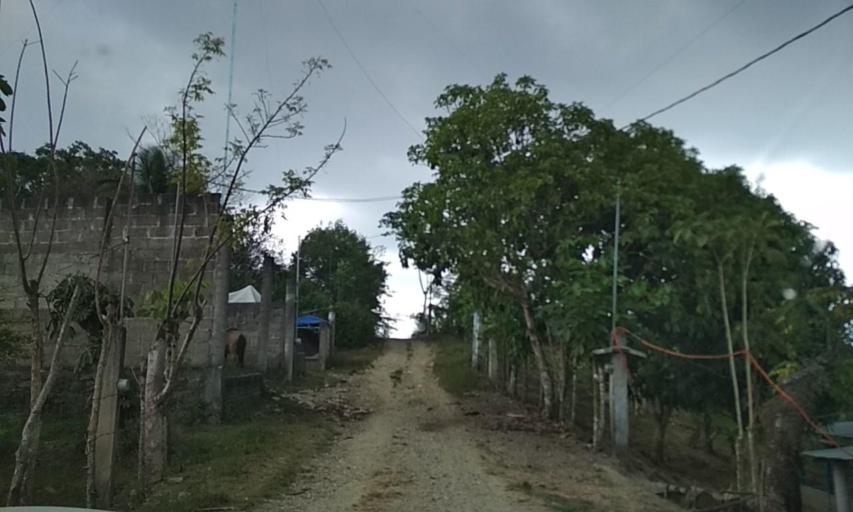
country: MX
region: Tabasco
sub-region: Huimanguillo
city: Francisco Rueda
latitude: 17.5644
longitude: -94.1130
